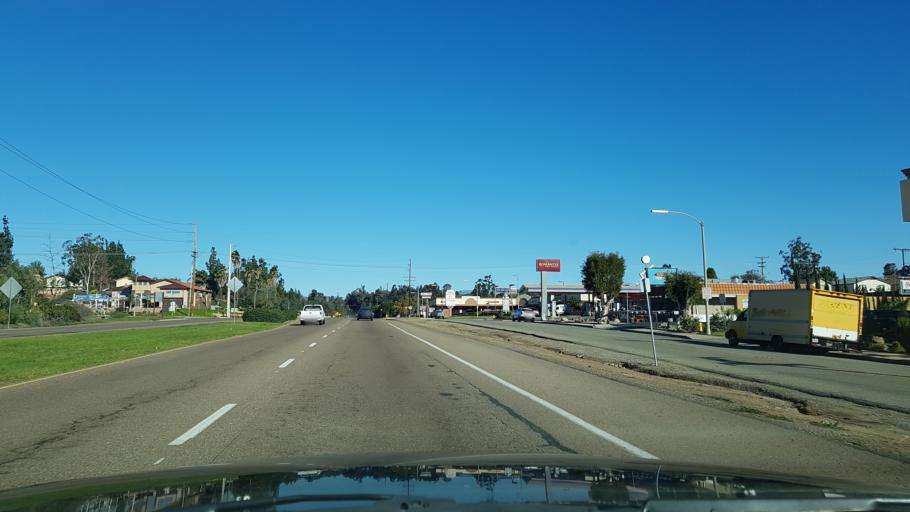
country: US
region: California
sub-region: San Diego County
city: Escondido
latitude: 33.0926
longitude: -117.0722
